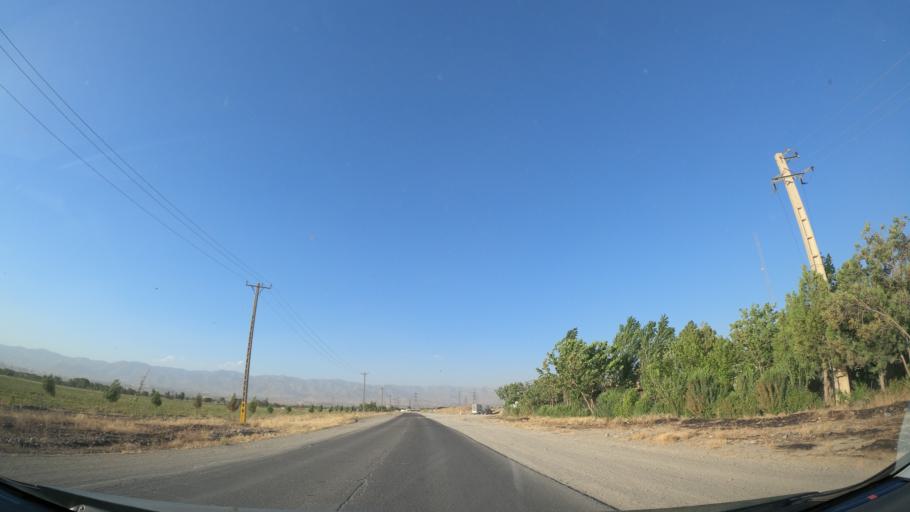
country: IR
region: Alborz
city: Hashtgerd
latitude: 35.9187
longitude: 50.7375
